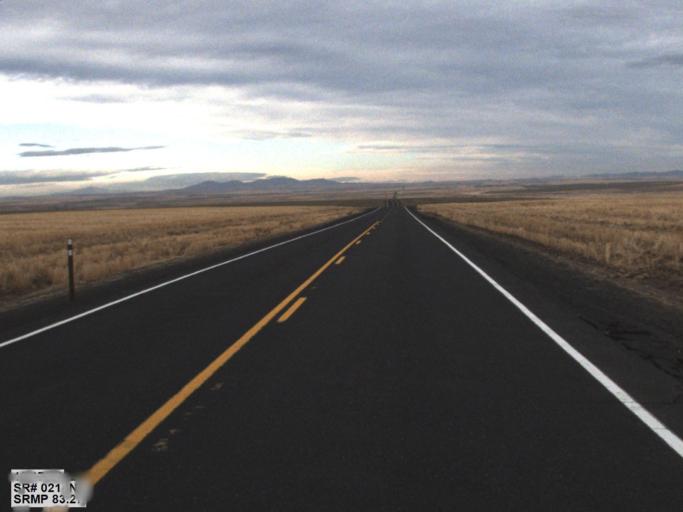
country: US
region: Washington
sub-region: Okanogan County
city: Coulee Dam
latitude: 47.6440
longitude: -118.7210
